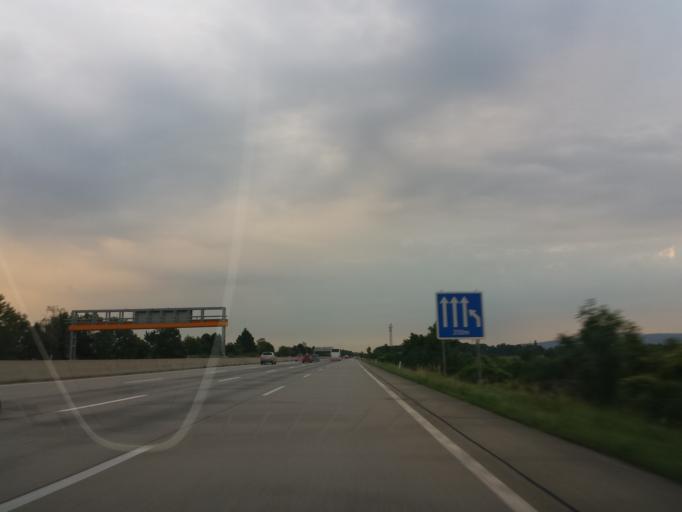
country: AT
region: Lower Austria
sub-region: Politischer Bezirk Neunkirchen
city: Breitenau
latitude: 47.7248
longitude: 16.1452
